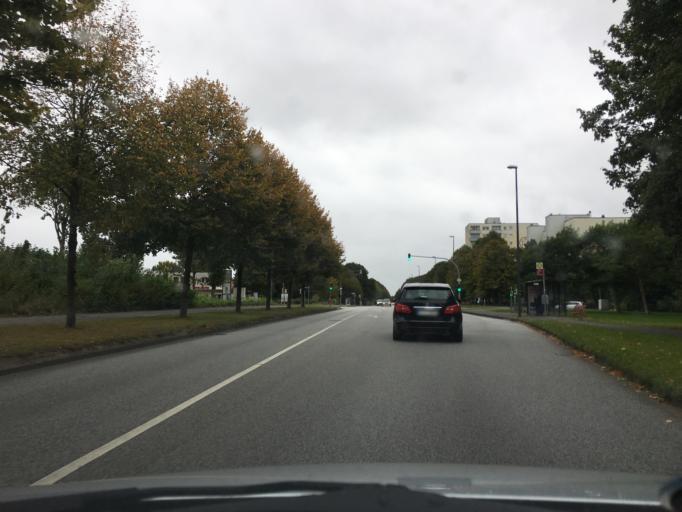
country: DE
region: Schleswig-Holstein
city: Kronshagen
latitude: 54.3256
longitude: 10.0613
